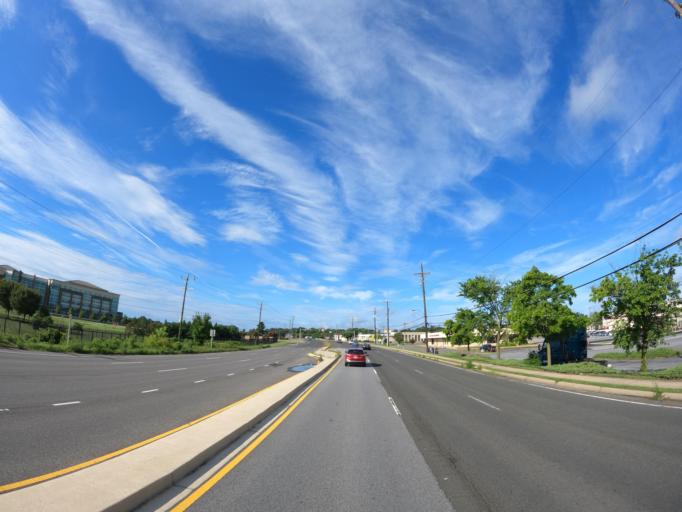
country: US
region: Maryland
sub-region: Prince George's County
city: Morningside
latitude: 38.8175
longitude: -76.8918
